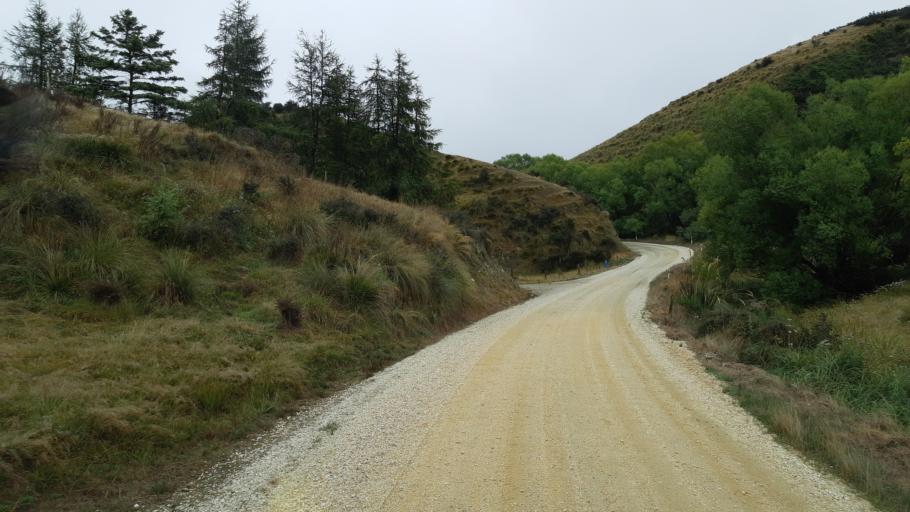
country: NZ
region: Otago
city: Oamaru
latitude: -44.9743
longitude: 170.5187
